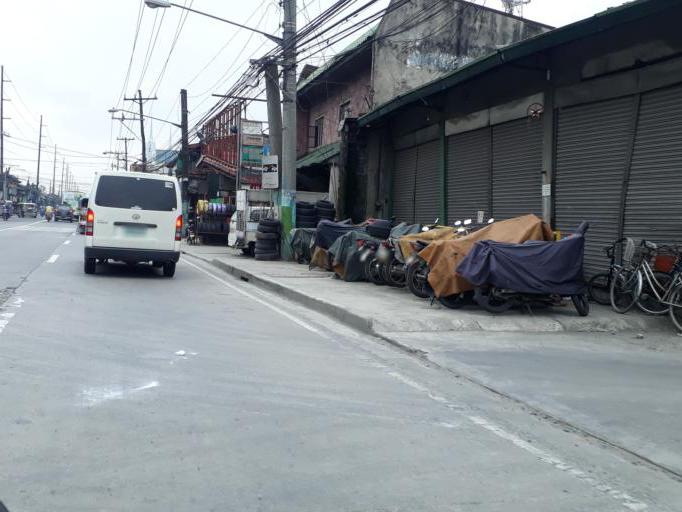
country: PH
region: Calabarzon
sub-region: Province of Rizal
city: Valenzuela
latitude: 14.7033
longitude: 120.9617
